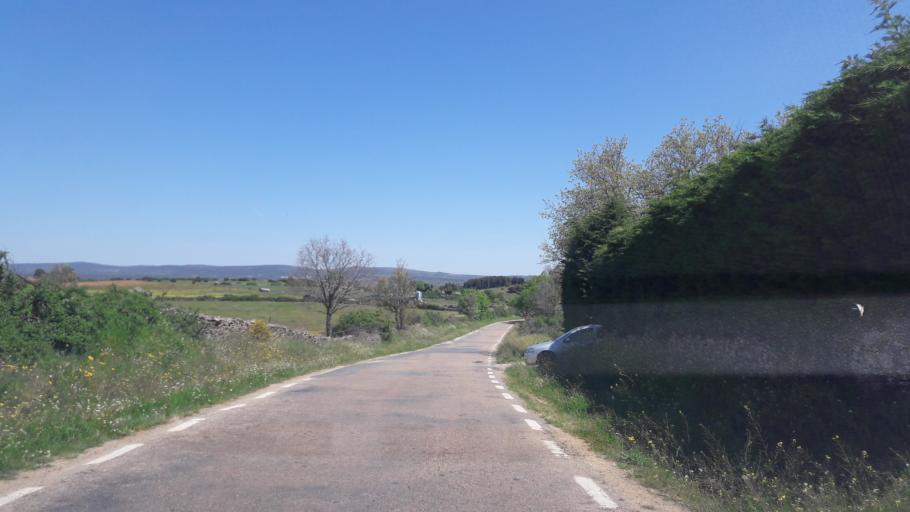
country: ES
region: Castille and Leon
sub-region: Provincia de Salamanca
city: Endrinal
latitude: 40.5823
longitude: -5.8081
